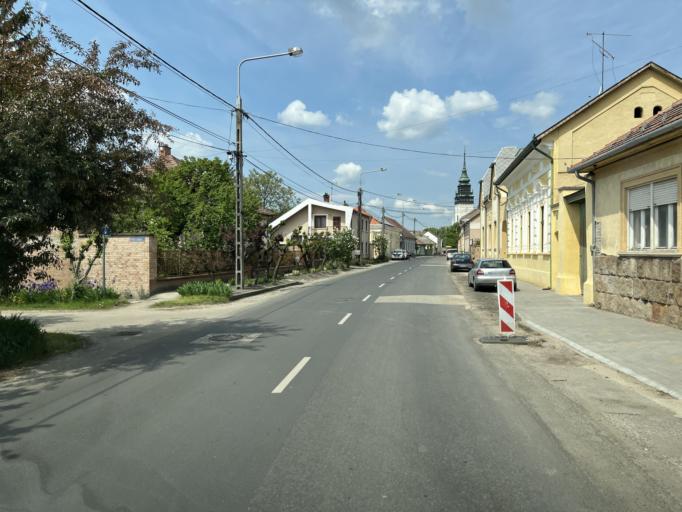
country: HU
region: Pest
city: Nagykoros
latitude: 47.0320
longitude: 19.7881
